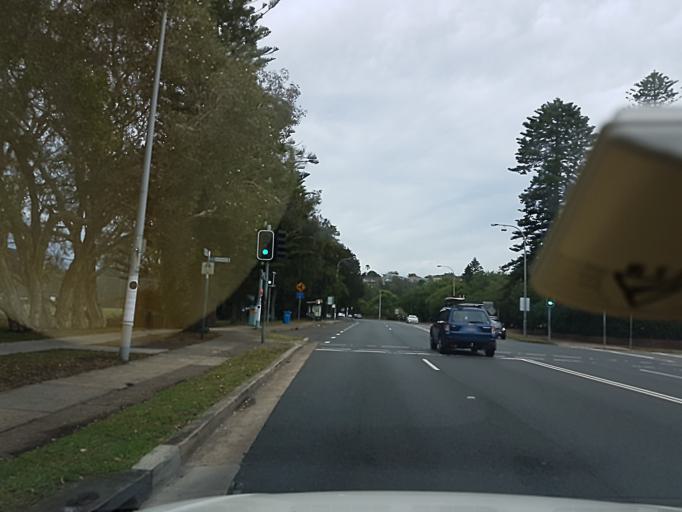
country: AU
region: New South Wales
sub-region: Warringah
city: Freshwater
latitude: -33.7859
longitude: 151.2809
